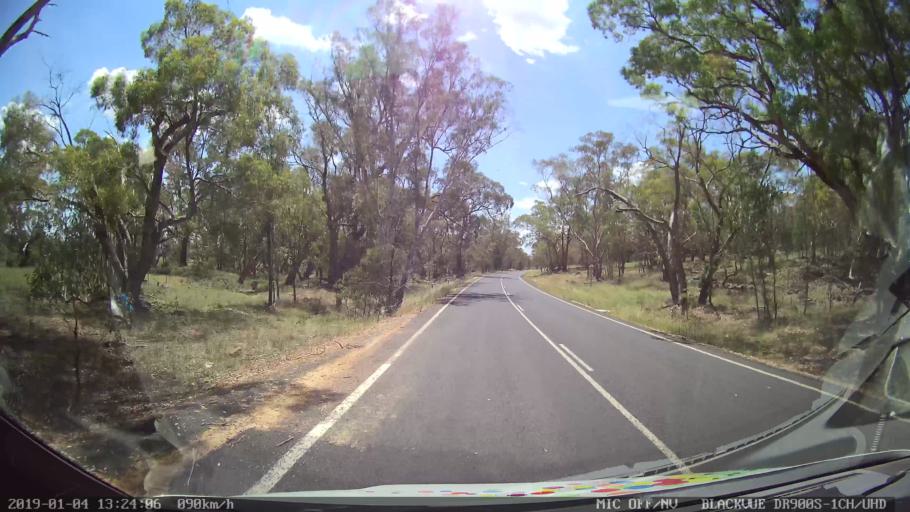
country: AU
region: New South Wales
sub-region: Parkes
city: Peak Hill
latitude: -32.7098
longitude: 148.5519
